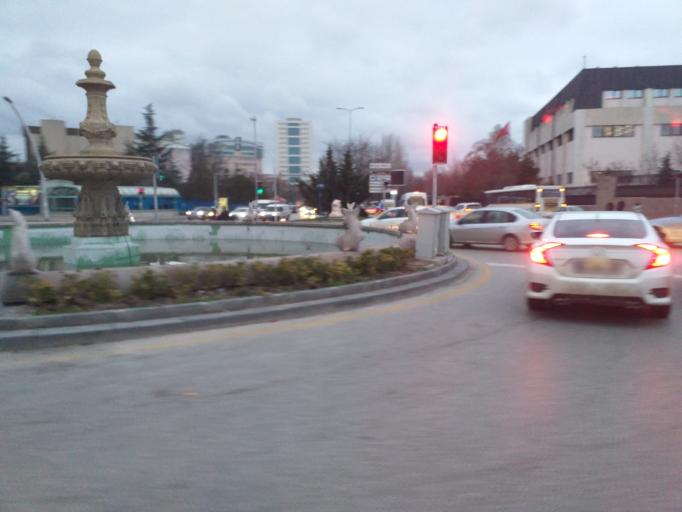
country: TR
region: Ankara
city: Ankara
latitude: 39.9328
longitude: 32.8294
